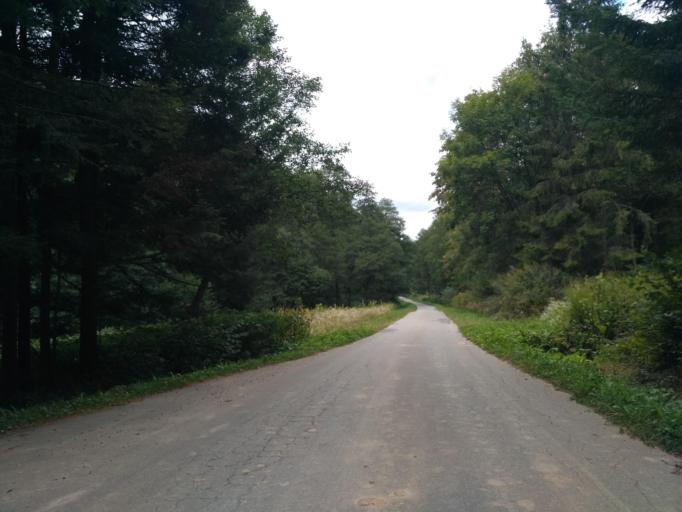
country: PL
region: Subcarpathian Voivodeship
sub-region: Powiat rzeszowski
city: Dynow
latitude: 49.7480
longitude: 22.2995
